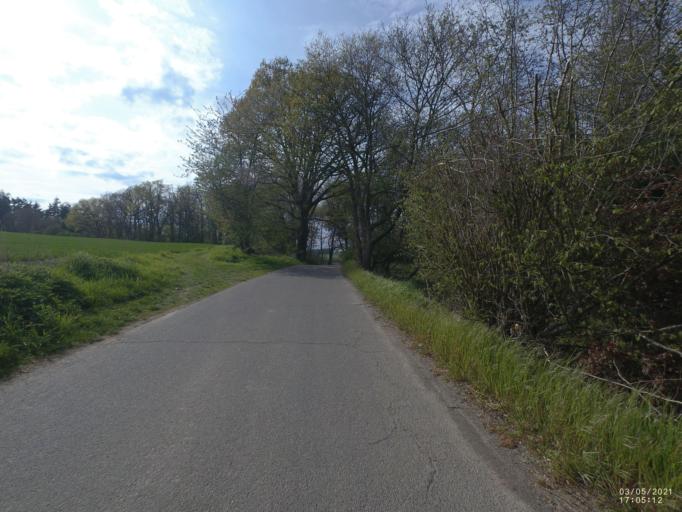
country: DE
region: Rheinland-Pfalz
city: Wolken
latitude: 50.3494
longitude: 7.4576
